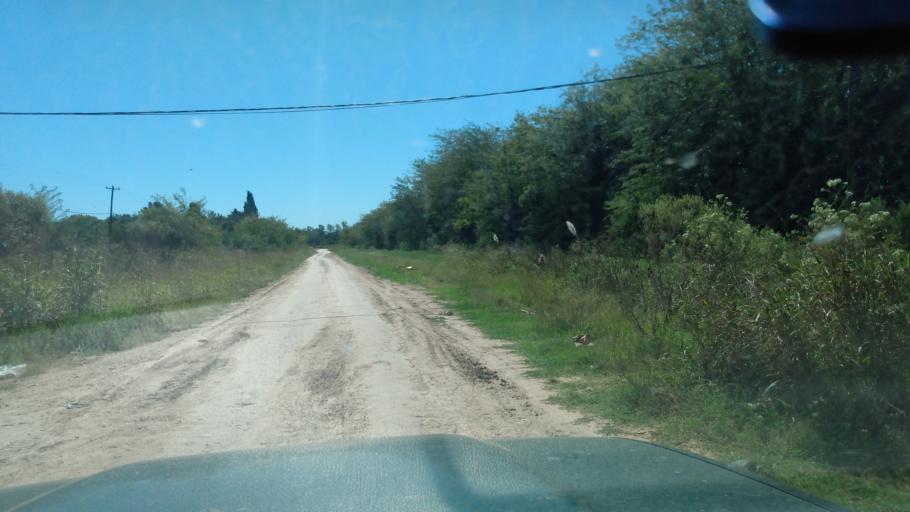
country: AR
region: Buenos Aires
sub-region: Partido de Lujan
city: Lujan
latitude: -34.5524
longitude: -59.1453
